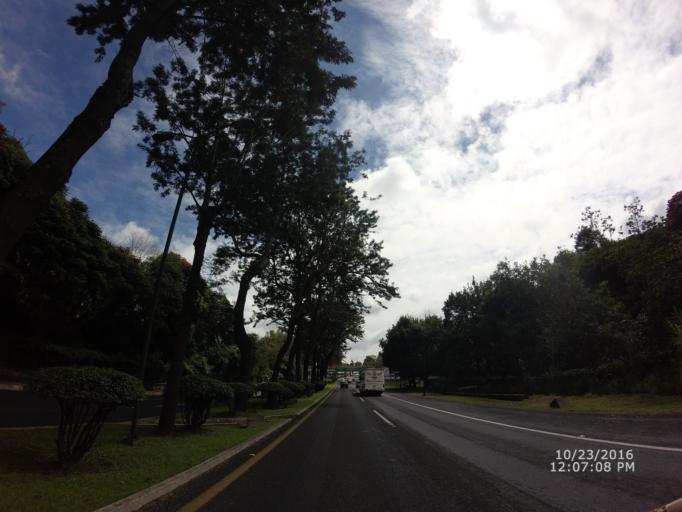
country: MX
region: Veracruz
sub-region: Xalapa
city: Lomas Verdes
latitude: 19.5208
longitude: -96.8868
